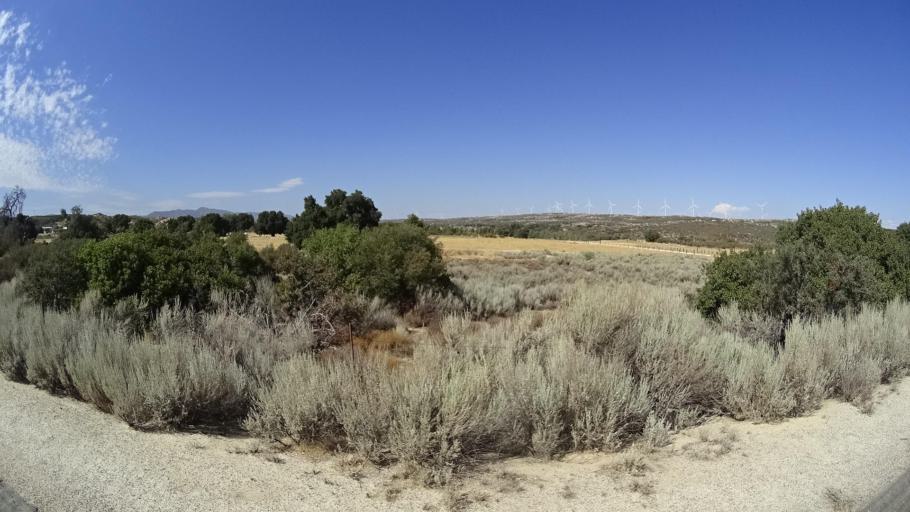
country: US
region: California
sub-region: San Diego County
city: Campo
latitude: 32.6994
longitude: -116.2944
